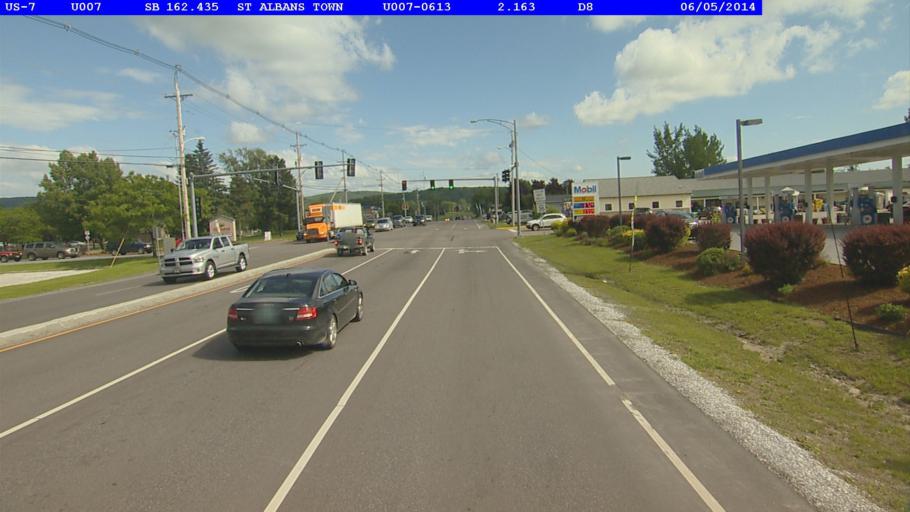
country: US
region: Vermont
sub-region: Franklin County
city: Saint Albans
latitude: 44.8393
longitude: -73.0826
